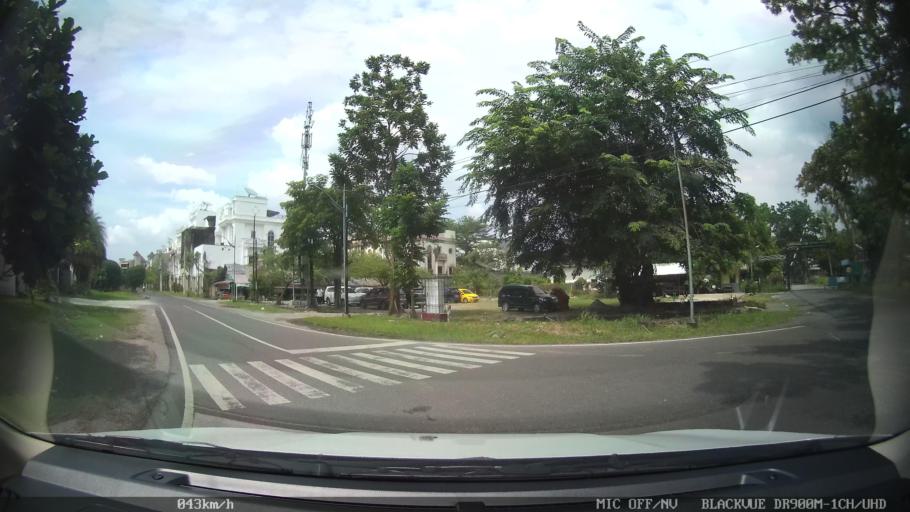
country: ID
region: North Sumatra
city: Medan
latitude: 3.5668
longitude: 98.6735
